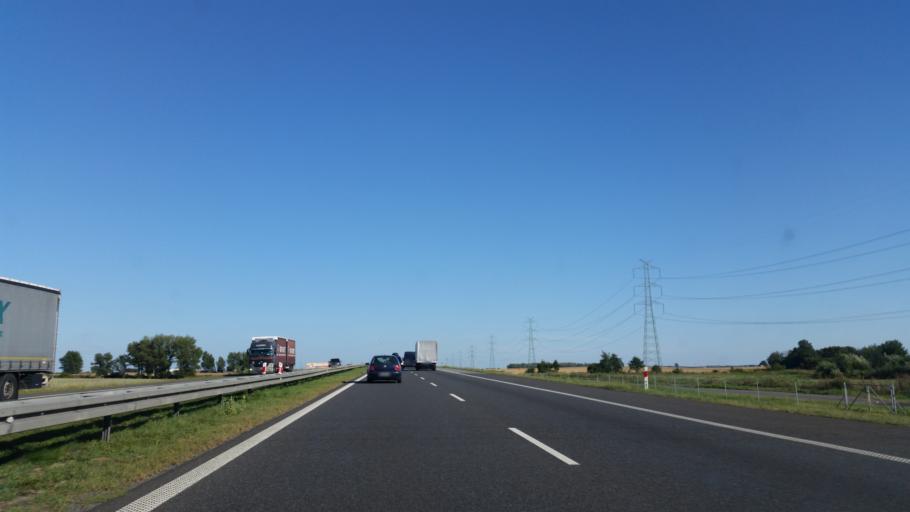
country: PL
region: Opole Voivodeship
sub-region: Powiat brzeski
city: Olszanka
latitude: 50.7589
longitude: 17.4258
